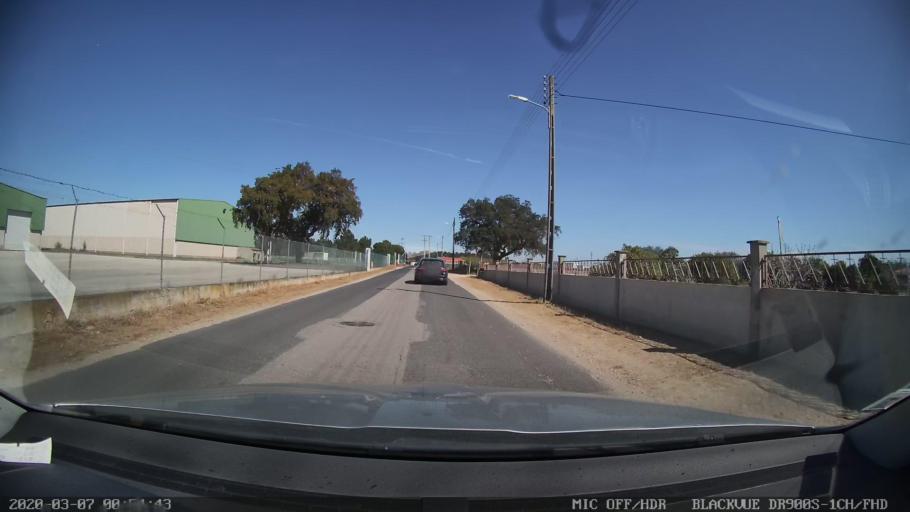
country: PT
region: Santarem
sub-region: Benavente
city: Benavente
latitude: 38.9537
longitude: -8.8186
